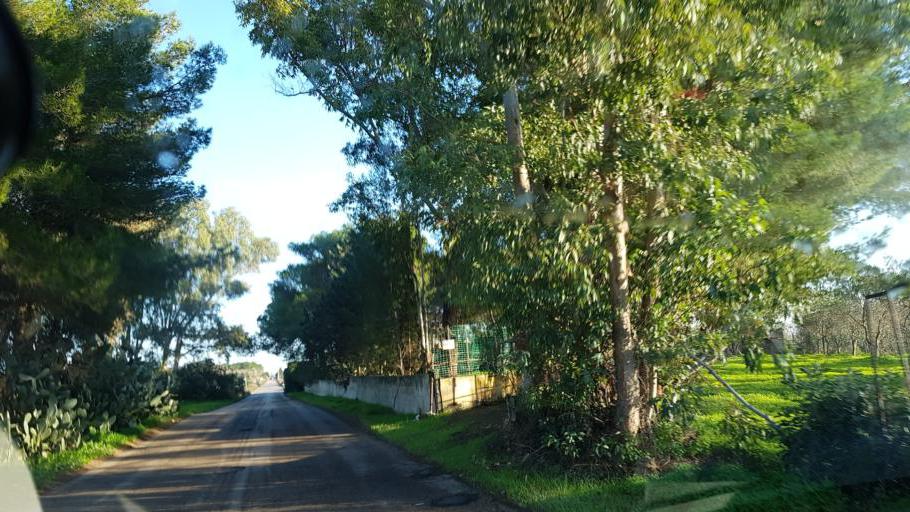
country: IT
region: Apulia
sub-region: Provincia di Brindisi
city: Torchiarolo
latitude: 40.5079
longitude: 18.0925
